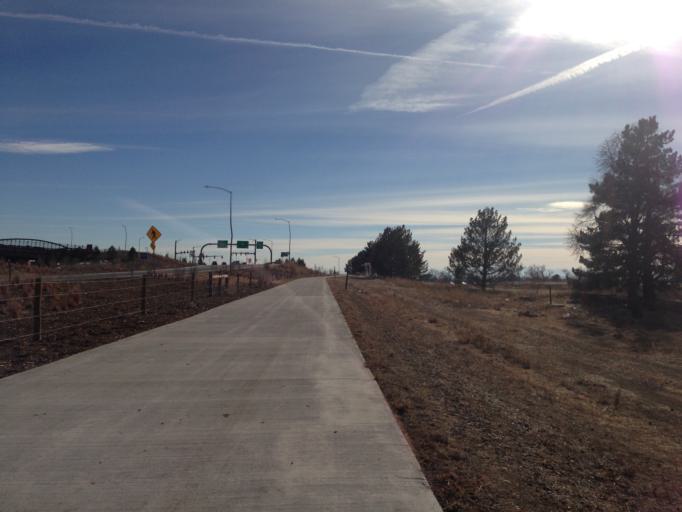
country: US
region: Colorado
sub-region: Adams County
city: Westminster
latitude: 39.8616
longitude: -105.0569
